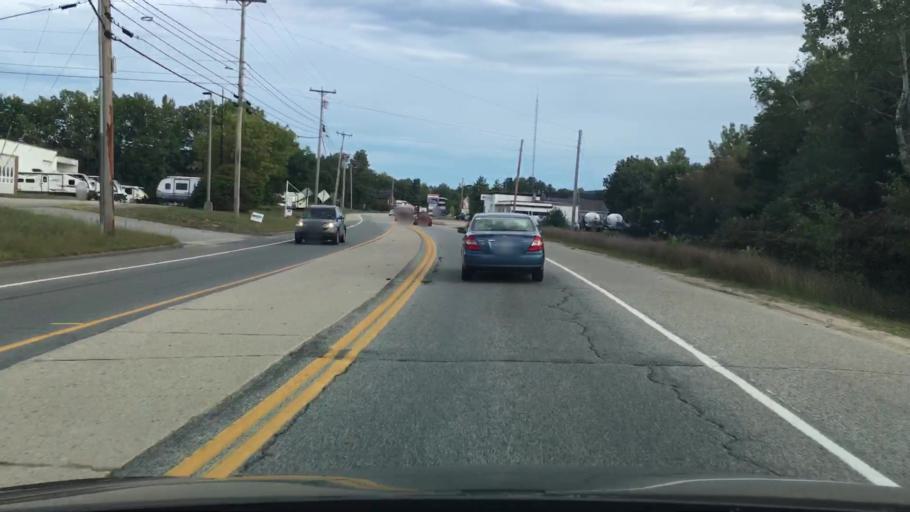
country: US
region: Maine
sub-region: Cumberland County
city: Bridgton
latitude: 44.0439
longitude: -70.7009
